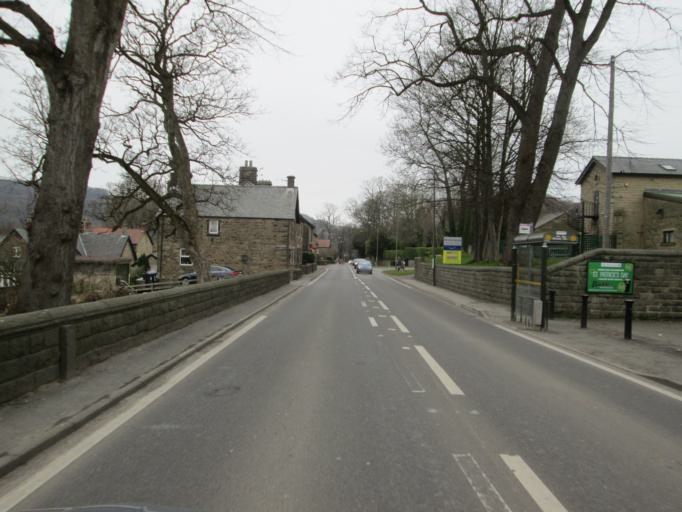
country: GB
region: England
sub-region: Derbyshire
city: Matlock
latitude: 53.1670
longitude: -1.5994
